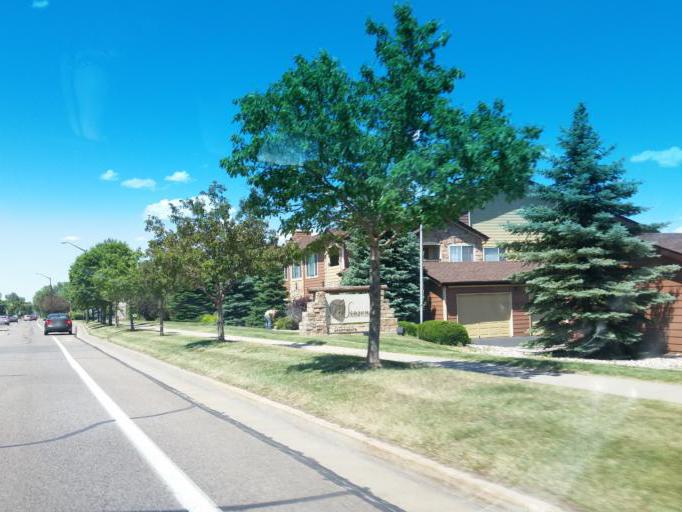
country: US
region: Colorado
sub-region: Larimer County
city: Fort Collins
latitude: 40.5351
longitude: -105.0960
